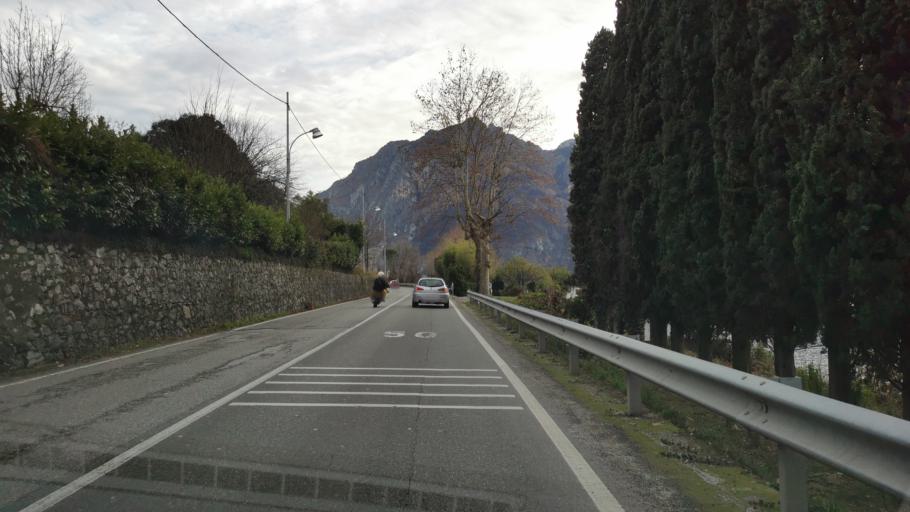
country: IT
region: Lombardy
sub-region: Provincia di Lecco
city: Abbadia Lariana
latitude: 45.9068
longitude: 9.3283
